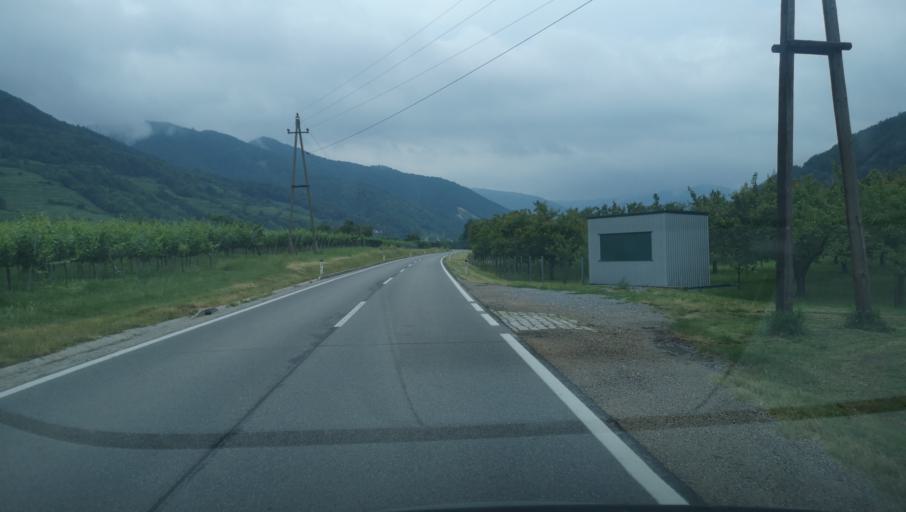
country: AT
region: Lower Austria
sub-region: Politischer Bezirk Krems
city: Aggsbach
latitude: 48.3265
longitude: 15.4066
